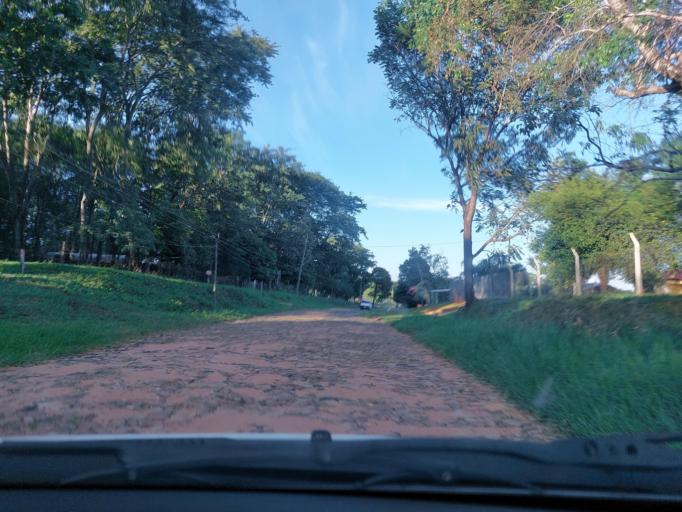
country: PY
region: San Pedro
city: Itacurubi del Rosario
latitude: -24.5614
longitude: -56.5915
